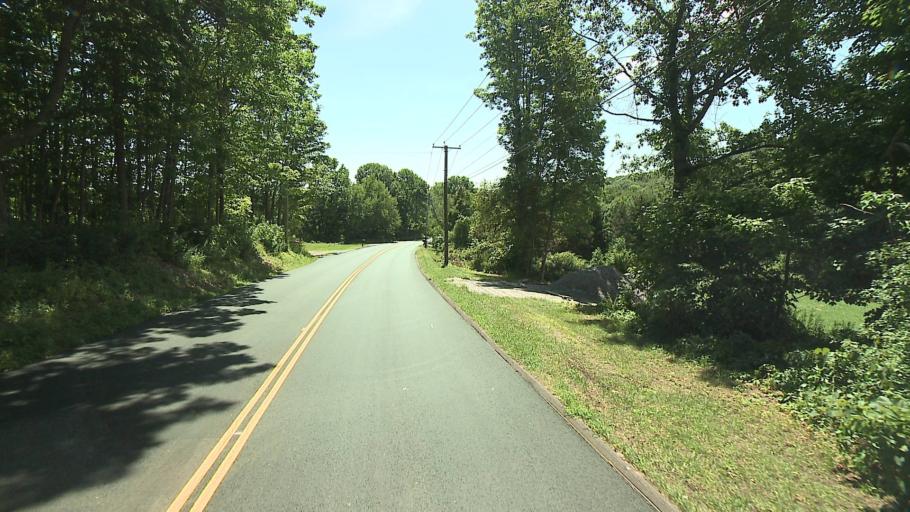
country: US
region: Connecticut
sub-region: Hartford County
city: West Simsbury
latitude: 41.9241
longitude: -72.9089
